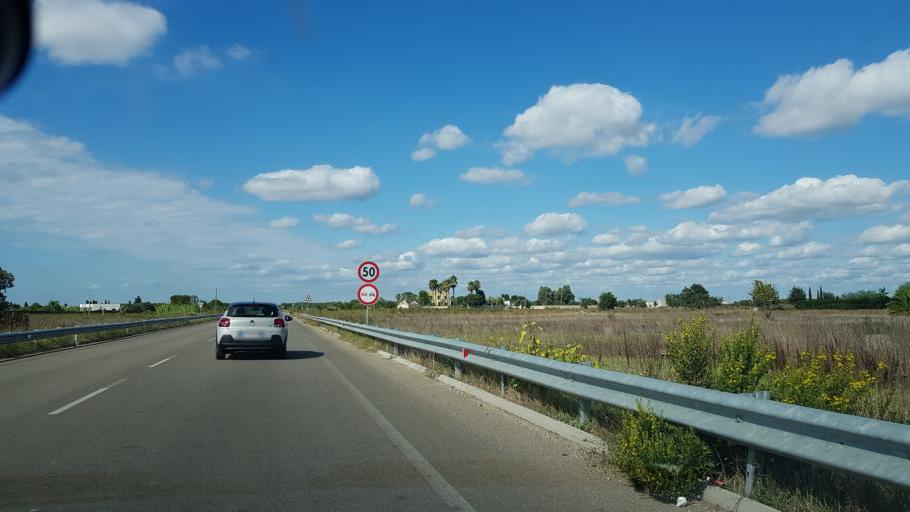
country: IT
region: Apulia
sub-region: Provincia di Lecce
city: Leverano
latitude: 40.3050
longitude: 18.0030
